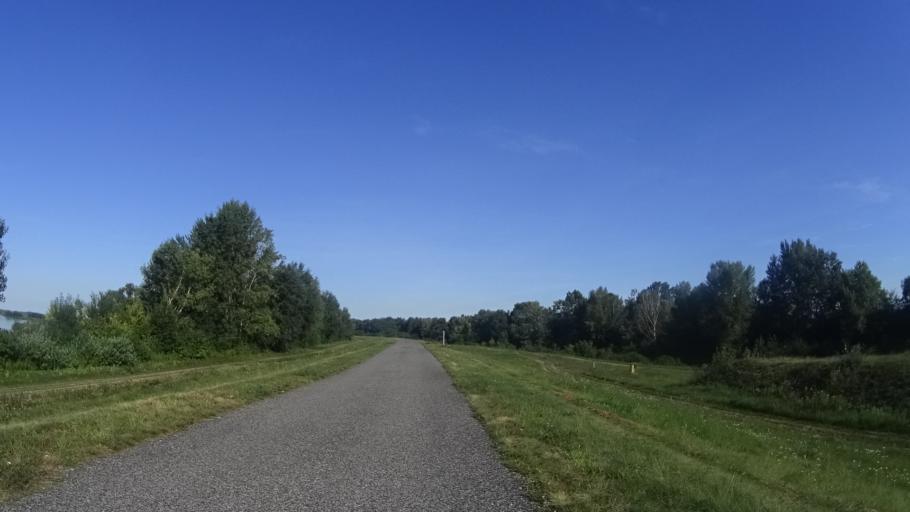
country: SK
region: Bratislavsky
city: Dunajska Luzna
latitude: 48.0538
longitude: 17.2331
